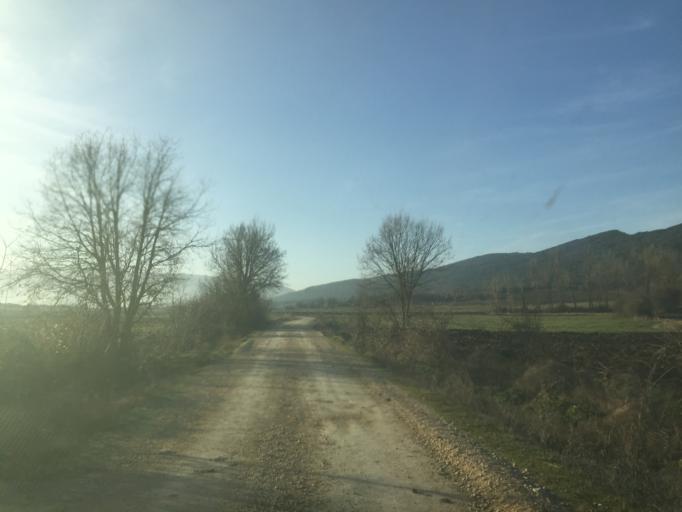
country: ES
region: Castille and Leon
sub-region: Provincia de Burgos
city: Medina de Pomar
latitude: 42.9378
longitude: -3.5945
